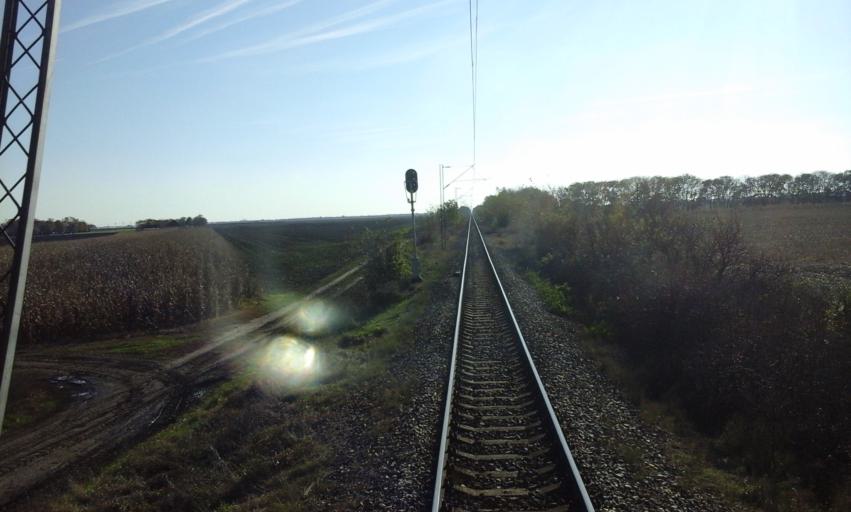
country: RS
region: Autonomna Pokrajina Vojvodina
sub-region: Severnobacki Okrug
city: Backa Topola
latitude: 45.8847
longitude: 19.6599
